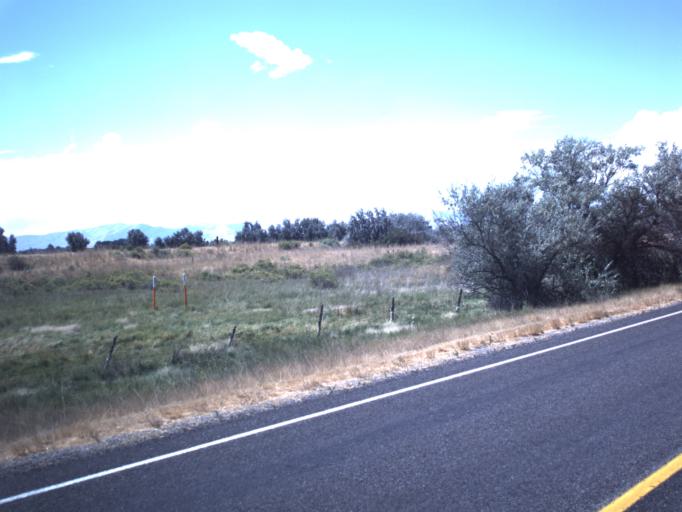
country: US
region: Utah
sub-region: Box Elder County
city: Honeyville
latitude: 41.5654
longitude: -112.1789
